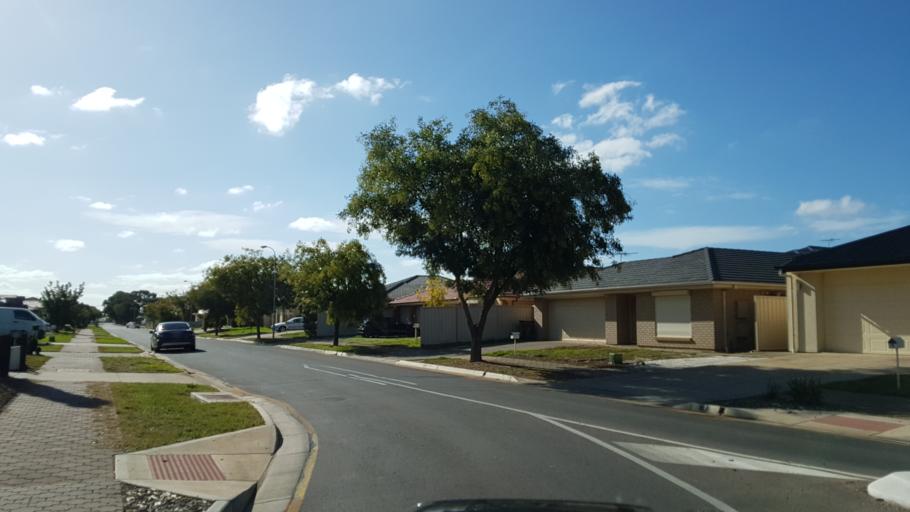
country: AU
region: South Australia
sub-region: Salisbury
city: Salisbury
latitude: -34.7666
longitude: 138.5992
